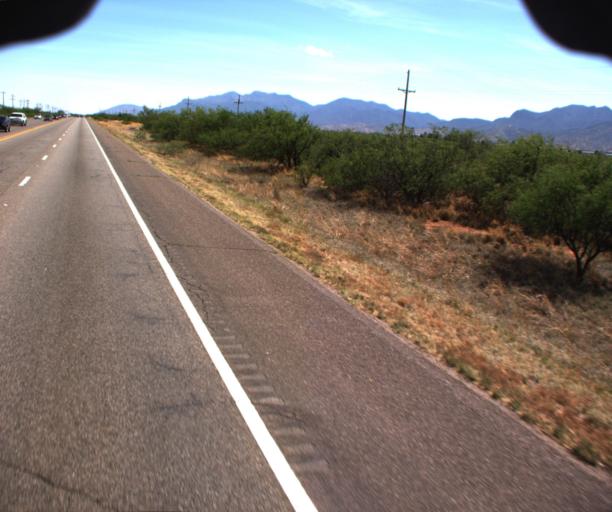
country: US
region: Arizona
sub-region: Cochise County
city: Huachuca City
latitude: 31.6016
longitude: -110.3280
